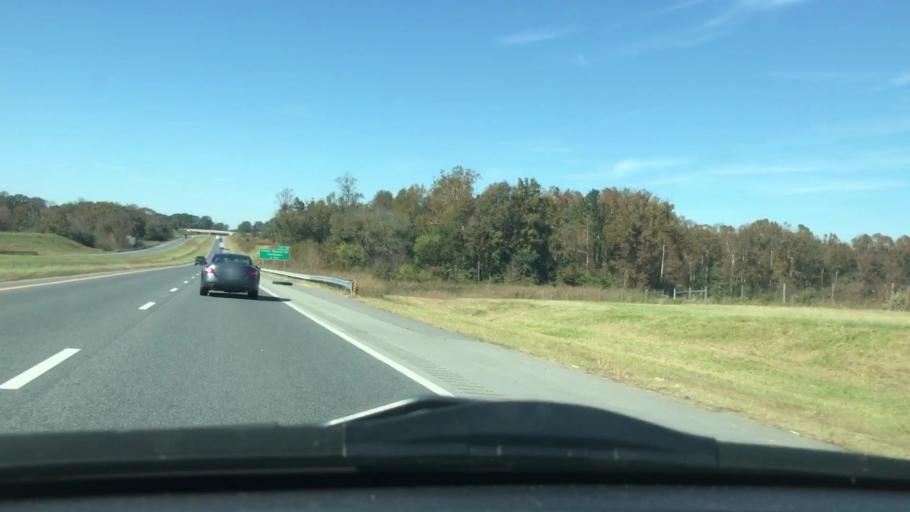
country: US
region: North Carolina
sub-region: Randolph County
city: Randleman
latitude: 35.8478
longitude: -79.8709
